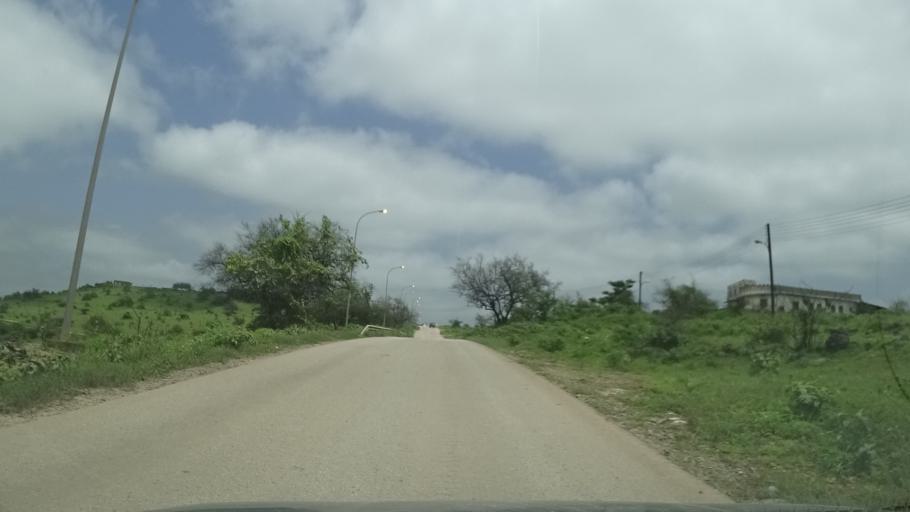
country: OM
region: Zufar
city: Salalah
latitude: 17.1852
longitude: 54.1602
